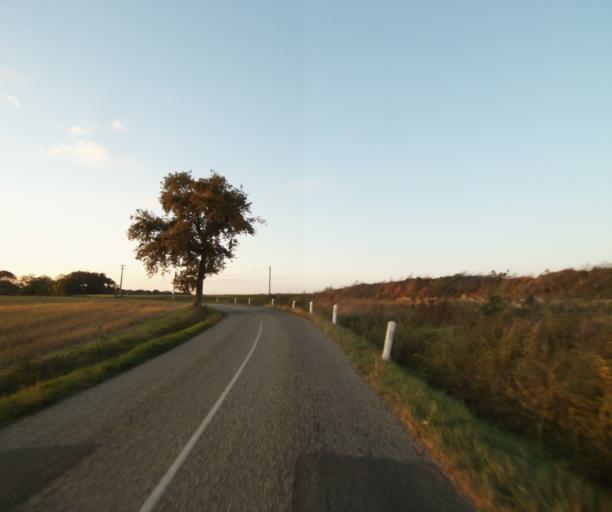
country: FR
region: Midi-Pyrenees
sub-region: Departement du Gers
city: Vic-Fezensac
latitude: 43.7958
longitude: 0.2470
